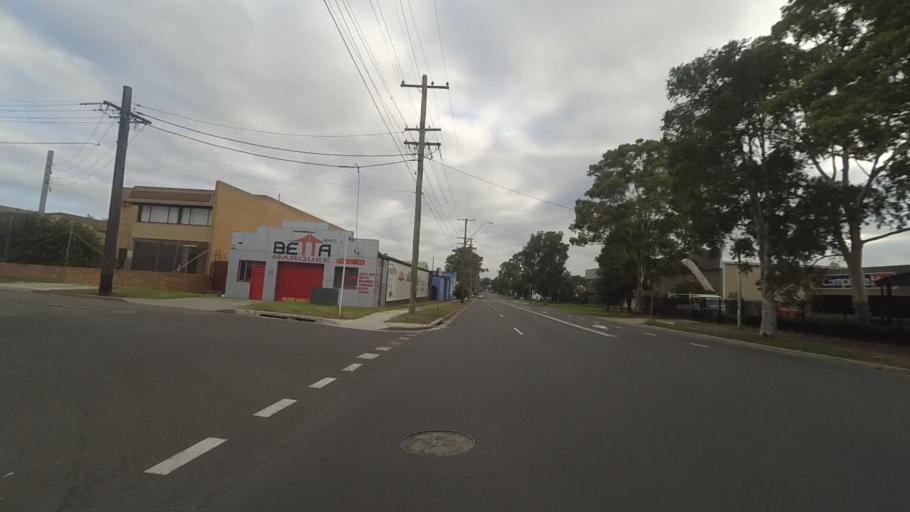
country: AU
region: New South Wales
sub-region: Bankstown
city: Revesby
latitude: -33.9317
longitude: 151.0122
